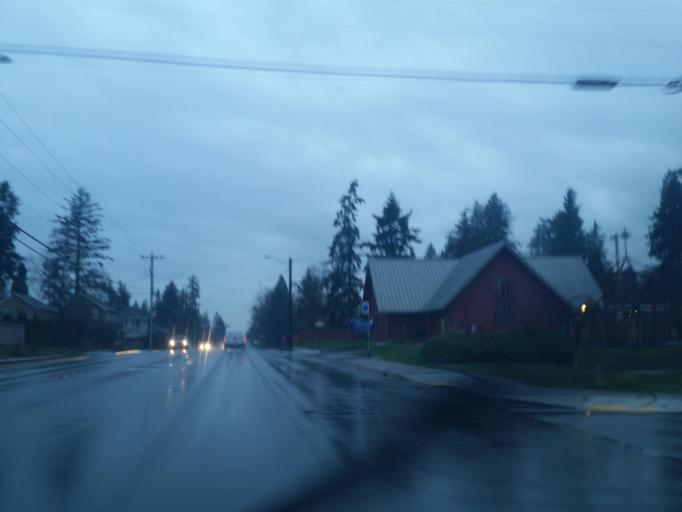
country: US
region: Washington
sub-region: Snohomish County
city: Meadowdale
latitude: 47.8608
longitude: -122.3037
